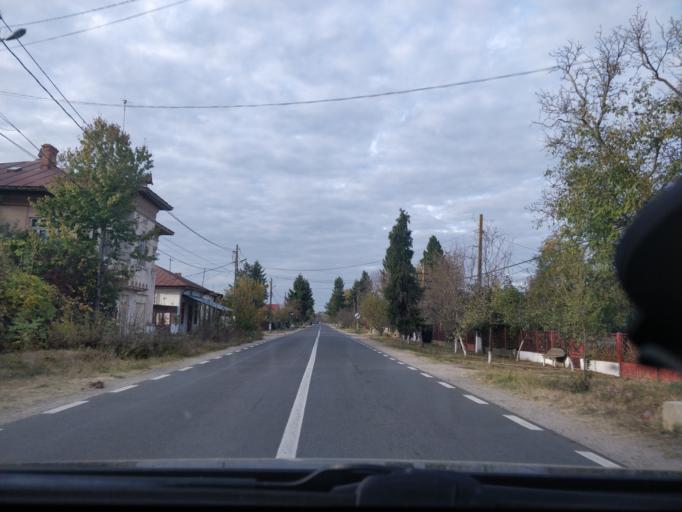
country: RO
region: Giurgiu
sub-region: Comuna Bucsani
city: Bucsani
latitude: 44.3703
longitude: 25.6590
